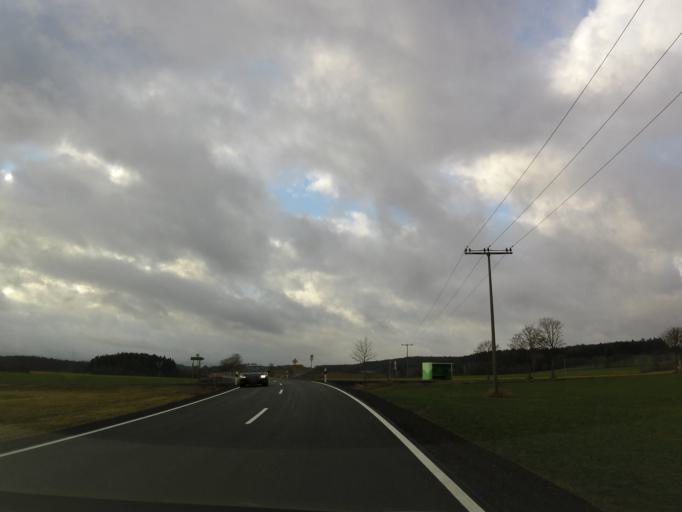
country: DE
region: Bavaria
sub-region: Upper Franconia
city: Hochstadt bei Thiersheim
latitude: 50.0758
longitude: 12.0774
